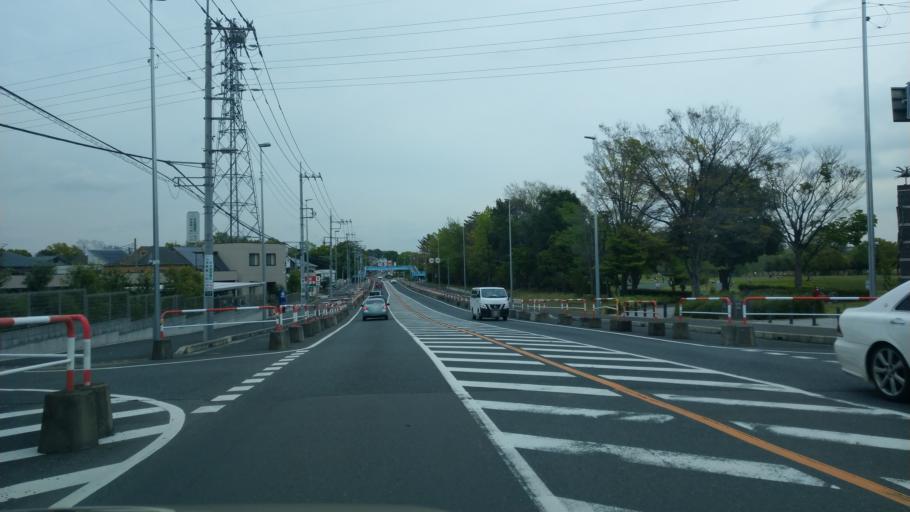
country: JP
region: Saitama
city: Saitama
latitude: 35.9145
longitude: 139.6394
